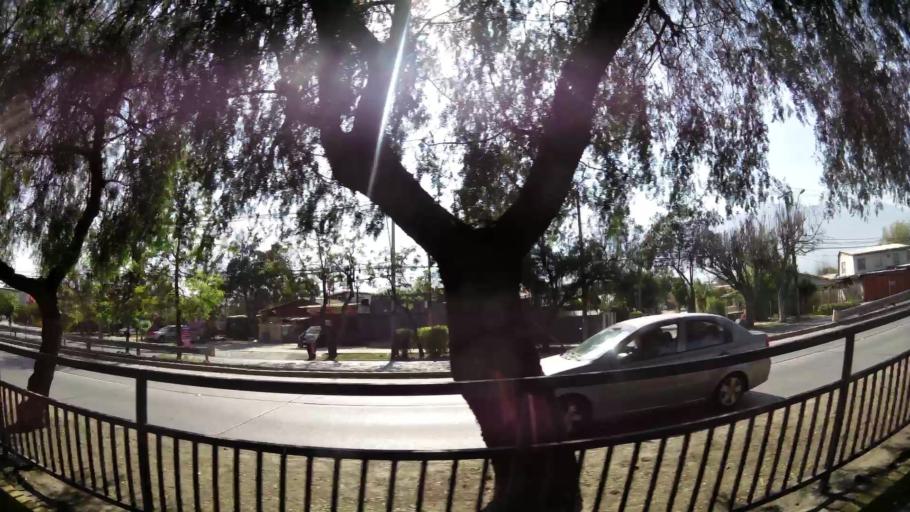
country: CL
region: Santiago Metropolitan
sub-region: Provincia de Santiago
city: Villa Presidente Frei, Nunoa, Santiago, Chile
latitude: -33.5206
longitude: -70.5797
